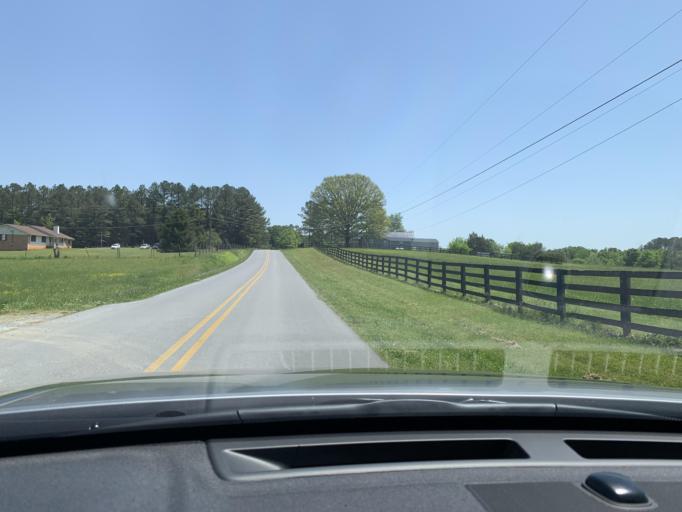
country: US
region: Georgia
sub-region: Polk County
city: Aragon
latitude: 34.0687
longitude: -85.0893
